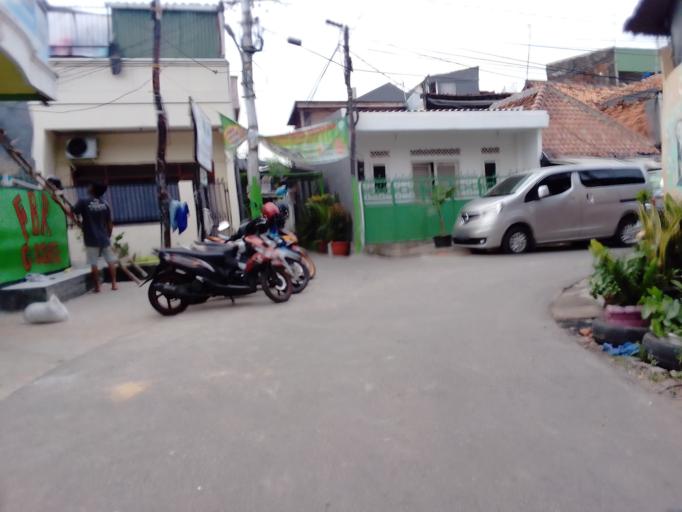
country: ID
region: Jakarta Raya
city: Jakarta
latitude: -6.1561
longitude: 106.8119
